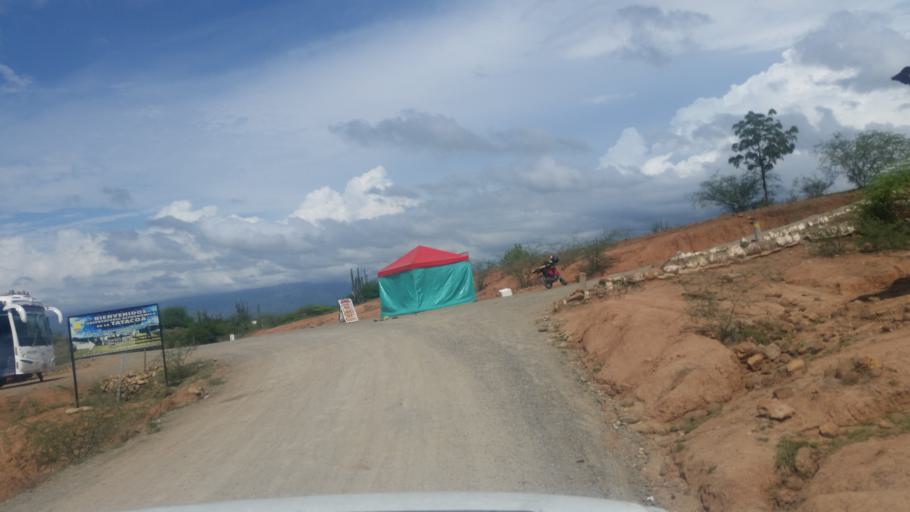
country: CO
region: Huila
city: Villavieja
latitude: 3.2338
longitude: -75.1703
